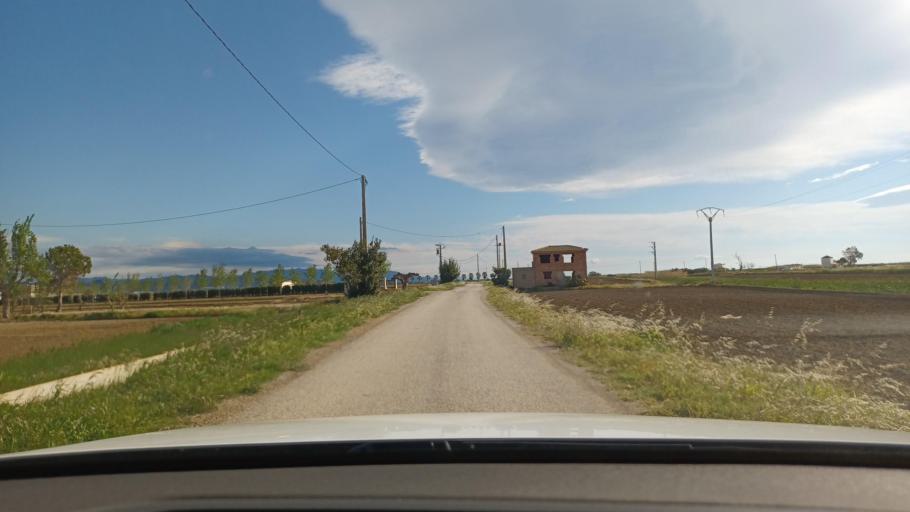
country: ES
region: Catalonia
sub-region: Provincia de Tarragona
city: L'Ampolla
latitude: 40.7749
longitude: 0.7113
